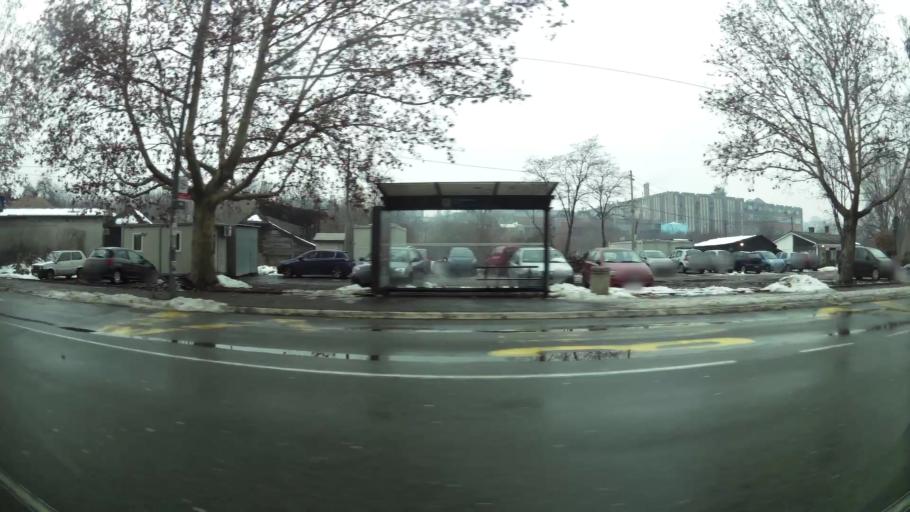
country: RS
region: Central Serbia
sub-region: Belgrade
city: Vozdovac
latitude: 44.7660
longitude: 20.4913
